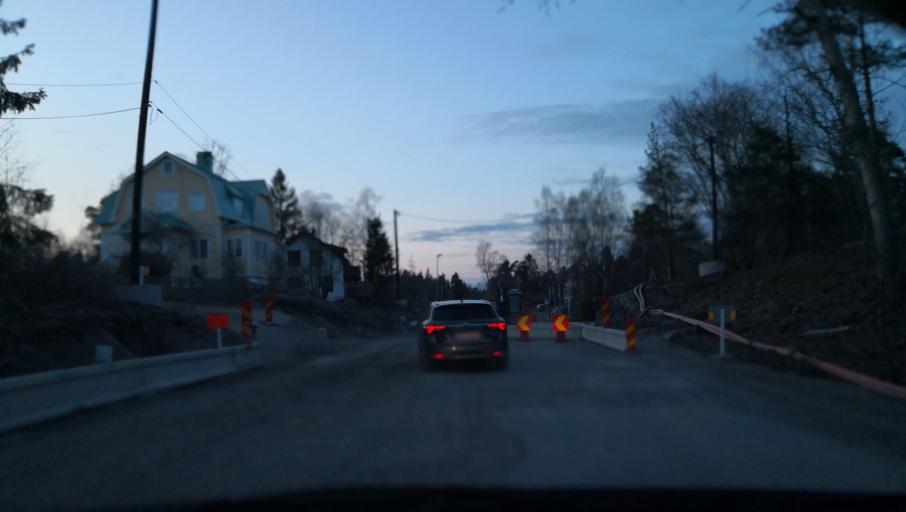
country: SE
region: Stockholm
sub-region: Nacka Kommun
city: Kummelnas
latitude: 59.3446
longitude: 18.2912
